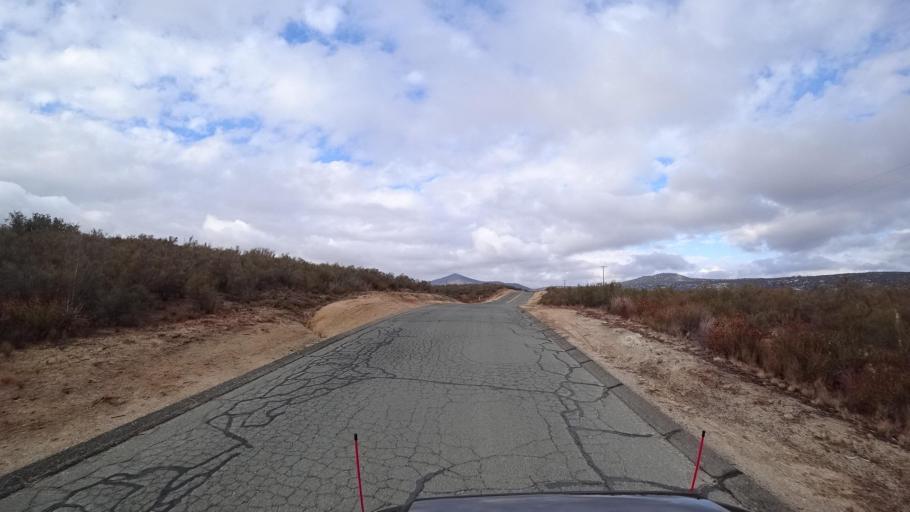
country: MX
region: Baja California
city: Tecate
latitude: 32.6290
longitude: -116.5812
